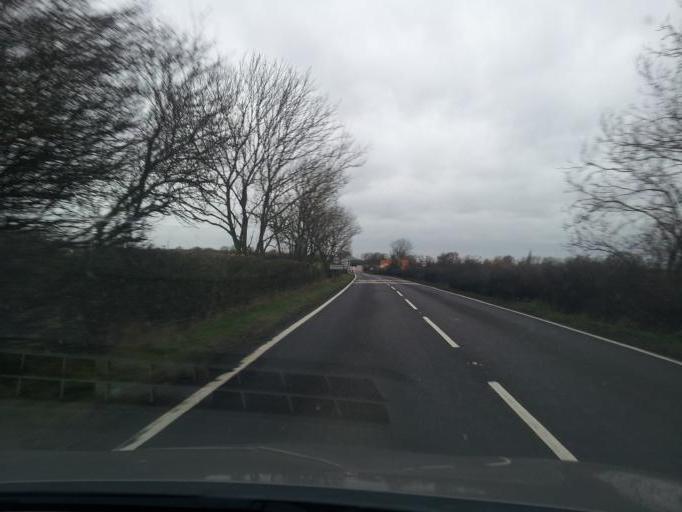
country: GB
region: England
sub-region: Suffolk
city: Botesdale
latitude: 52.3293
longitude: 0.9268
